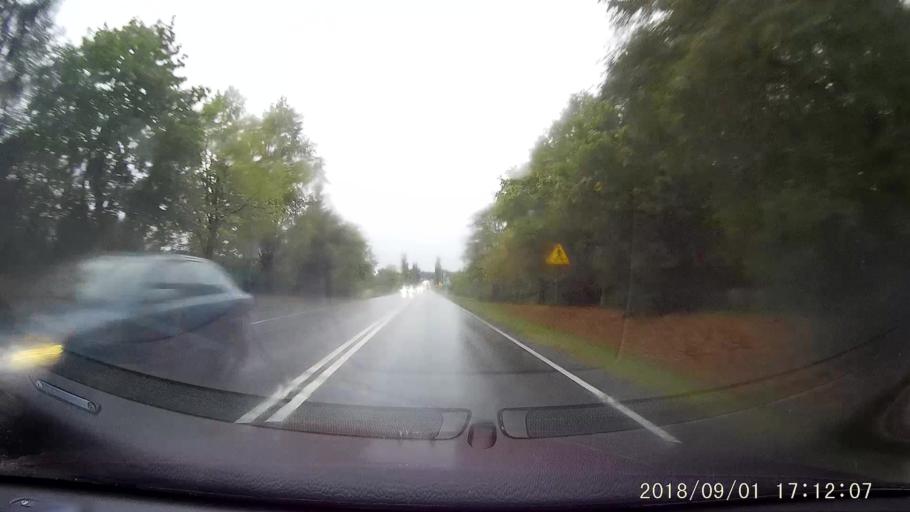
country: PL
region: Lubusz
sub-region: Powiat zielonogorski
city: Nowogrod Bobrzanski
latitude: 51.8030
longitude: 15.2560
